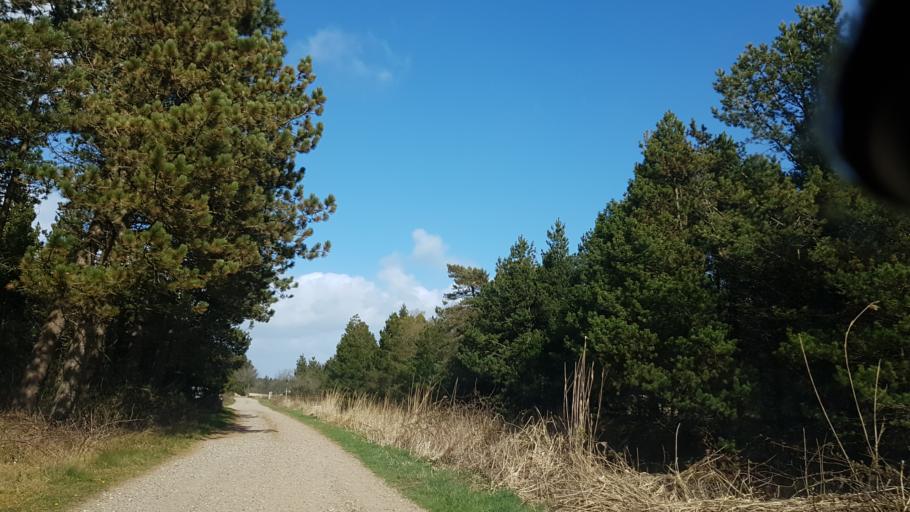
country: DE
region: Schleswig-Holstein
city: List
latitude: 55.0843
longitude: 8.5352
